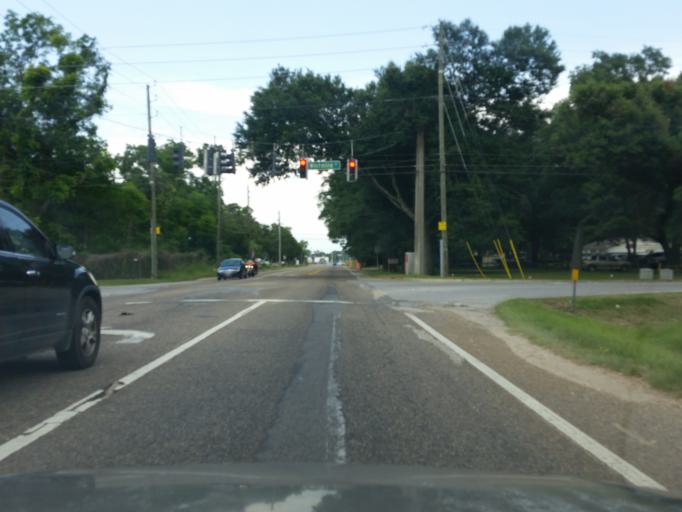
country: US
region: Florida
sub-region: Escambia County
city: Ferry Pass
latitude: 30.5106
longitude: -87.2273
